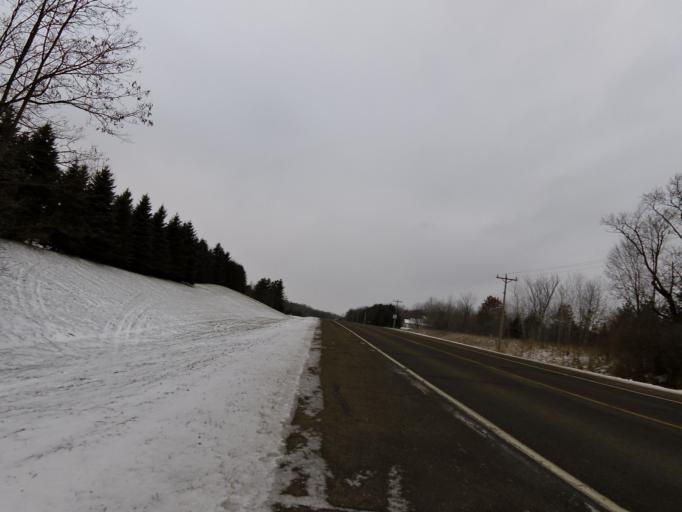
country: US
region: Minnesota
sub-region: Washington County
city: Lake Elmo
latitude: 44.9634
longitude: -92.8278
